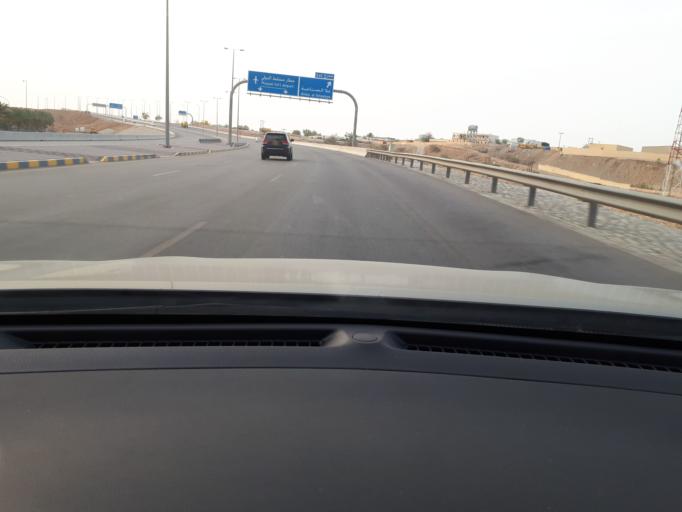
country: OM
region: Muhafazat Masqat
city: Bawshar
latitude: 23.5647
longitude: 58.3385
